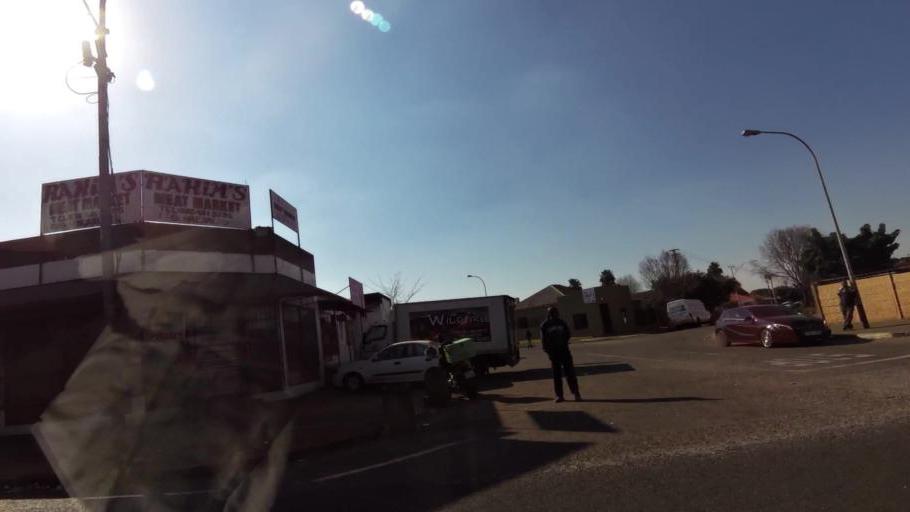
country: ZA
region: Gauteng
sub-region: City of Johannesburg Metropolitan Municipality
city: Johannesburg
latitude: -26.1739
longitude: 27.9640
